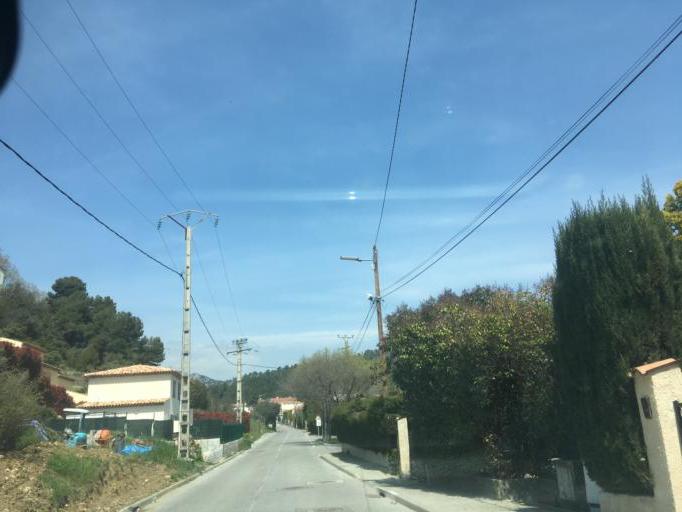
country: FR
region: Provence-Alpes-Cote d'Azur
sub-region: Departement des Alpes-Maritimes
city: Levens
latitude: 43.8562
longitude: 7.2275
